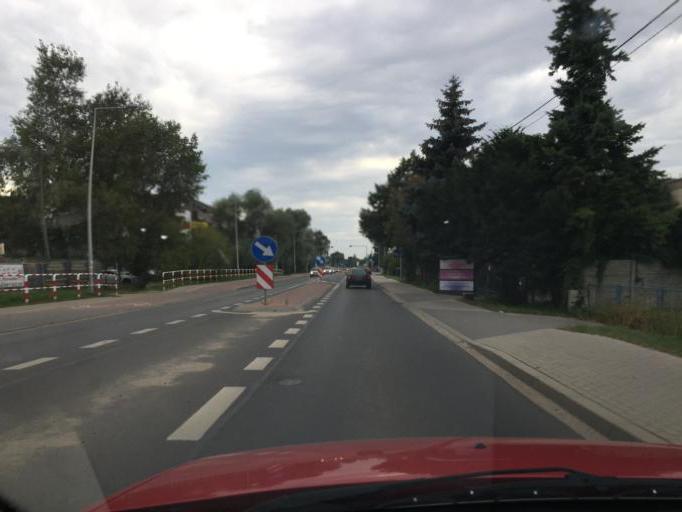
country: PL
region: Greater Poland Voivodeship
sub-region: Powiat poznanski
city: Plewiska
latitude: 52.3957
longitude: 16.7995
